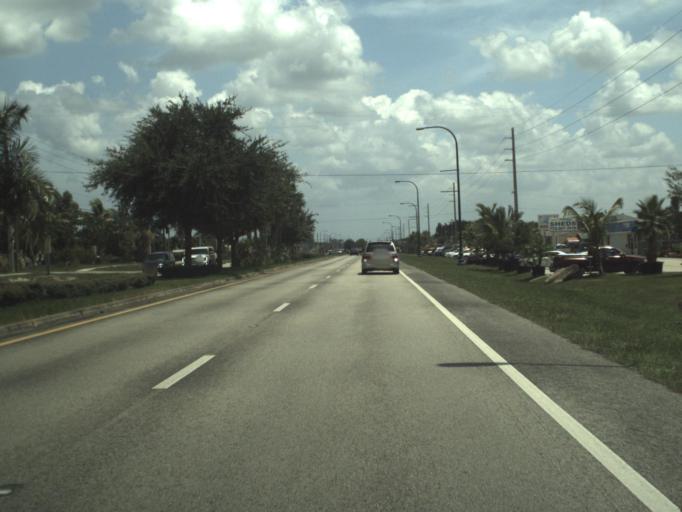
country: US
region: Florida
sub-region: Martin County
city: Hobe Sound
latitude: 27.0696
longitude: -80.1411
